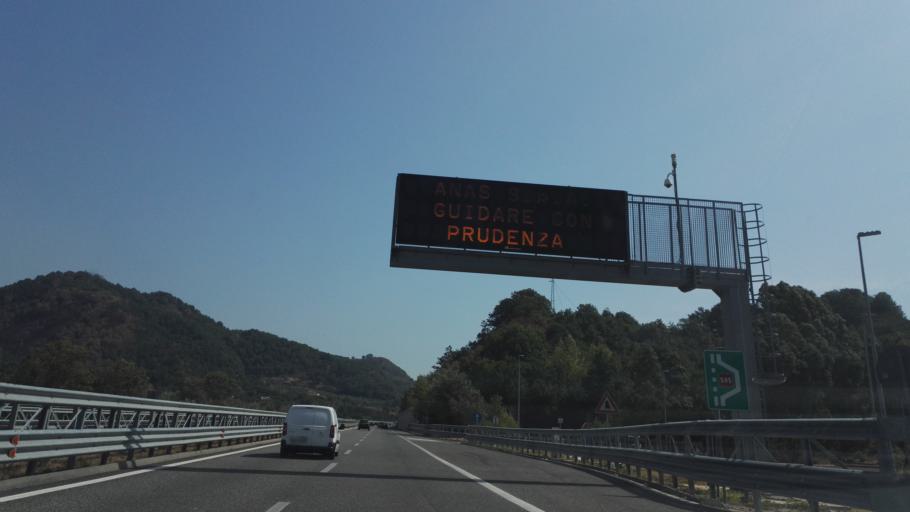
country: IT
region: Calabria
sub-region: Provincia di Catanzaro
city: Martirano Lombardo
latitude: 39.0848
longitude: 16.2192
